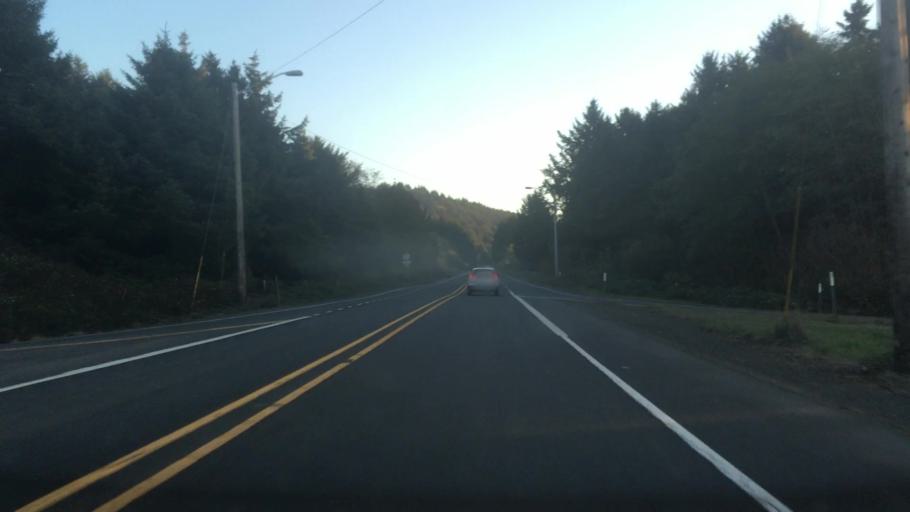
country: US
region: Oregon
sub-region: Clatsop County
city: Cannon Beach
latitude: 45.8712
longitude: -123.9583
